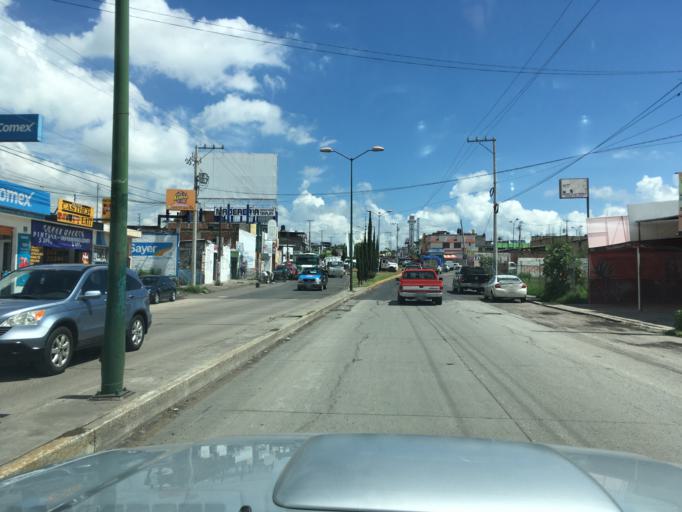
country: MX
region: Michoacan
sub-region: Tarimbaro
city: Real Hacienda (Metropolis)
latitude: 19.7282
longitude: -101.1981
